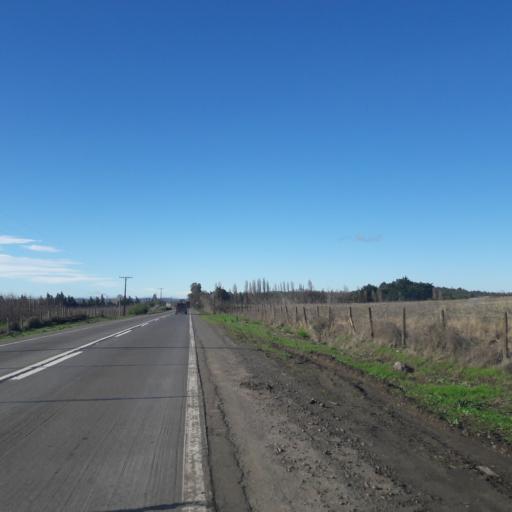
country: CL
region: Araucania
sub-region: Provincia de Malleco
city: Angol
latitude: -37.7469
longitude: -72.5945
